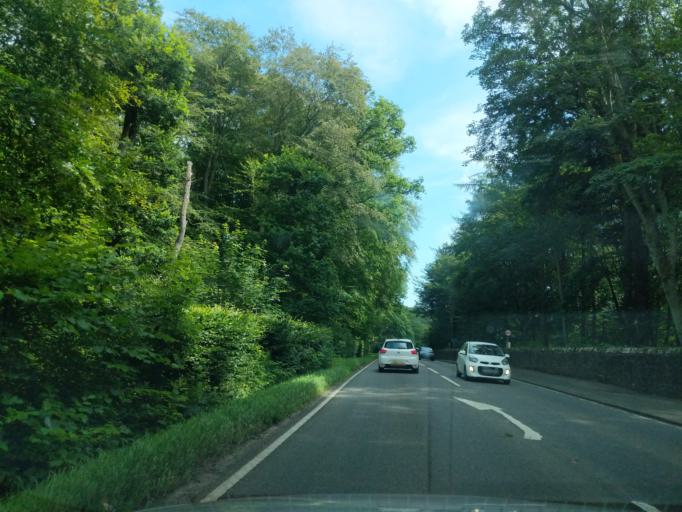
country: GB
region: Scotland
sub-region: Angus
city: Muirhead
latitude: 56.4878
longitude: -3.0388
